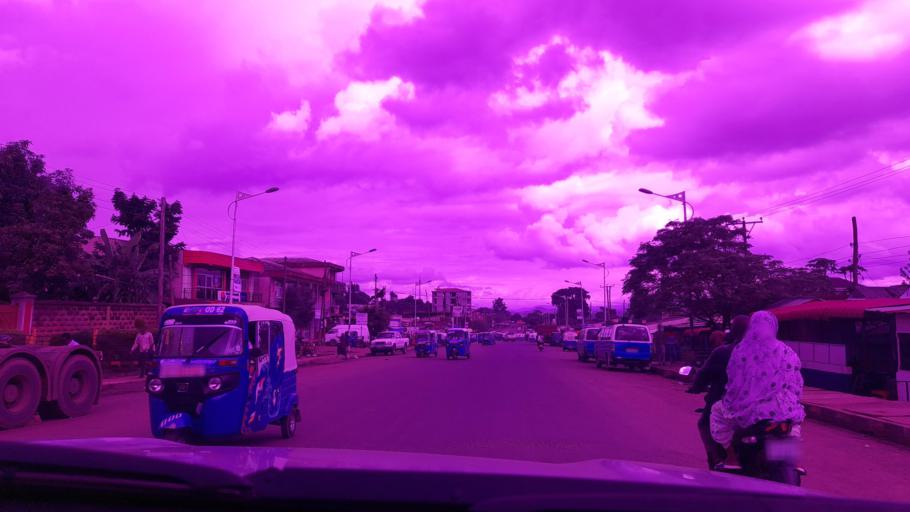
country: ET
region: Oromiya
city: Jima
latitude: 7.6739
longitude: 36.8537
